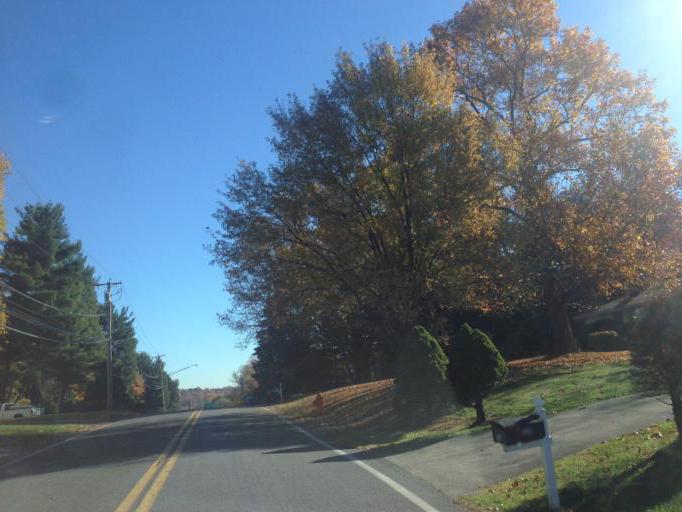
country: US
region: Maryland
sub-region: Howard County
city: Riverside
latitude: 39.1989
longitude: -76.8659
